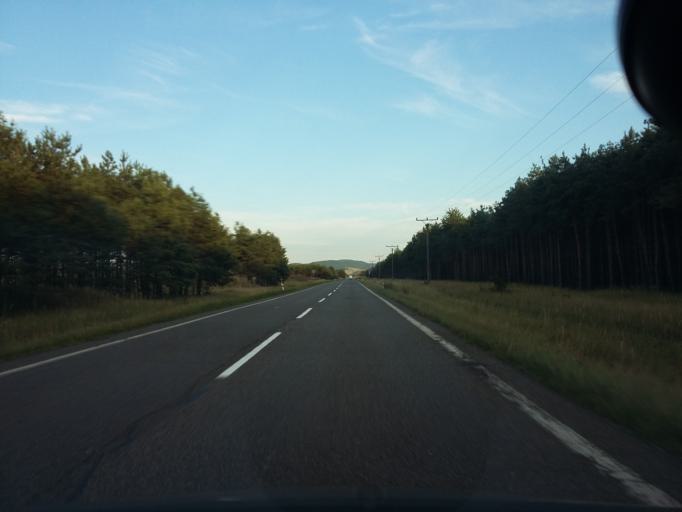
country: SK
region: Bratislavsky
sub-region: Okres Malacky
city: Malacky
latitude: 48.4229
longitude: 17.0523
